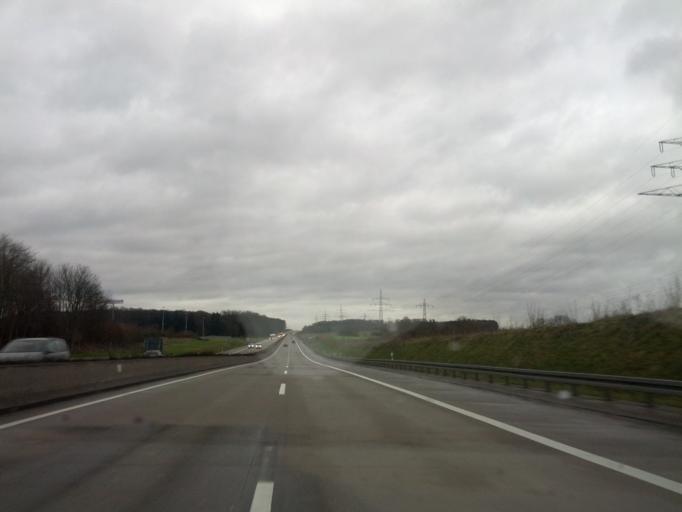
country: DE
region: Hesse
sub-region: Regierungsbezirk Giessen
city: Lich
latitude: 50.5522
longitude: 8.7872
